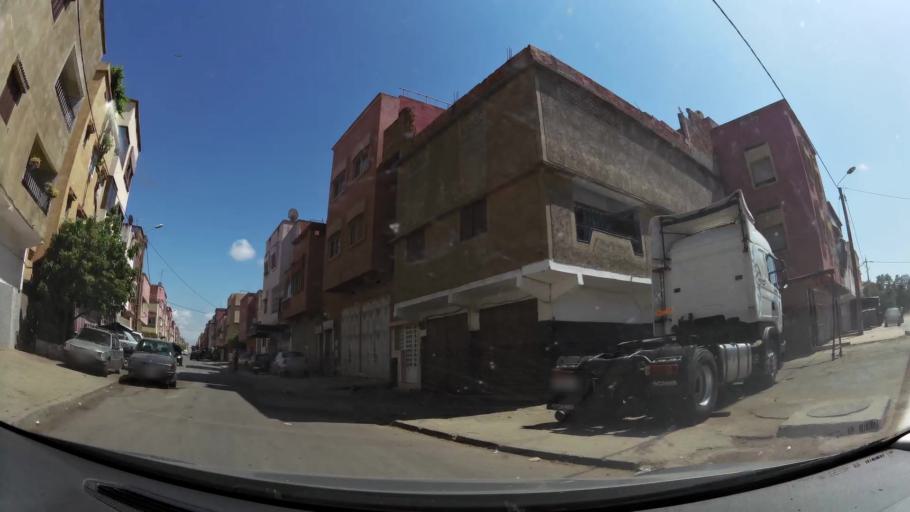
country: MA
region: Gharb-Chrarda-Beni Hssen
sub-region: Kenitra Province
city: Kenitra
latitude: 34.2437
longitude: -6.5551
